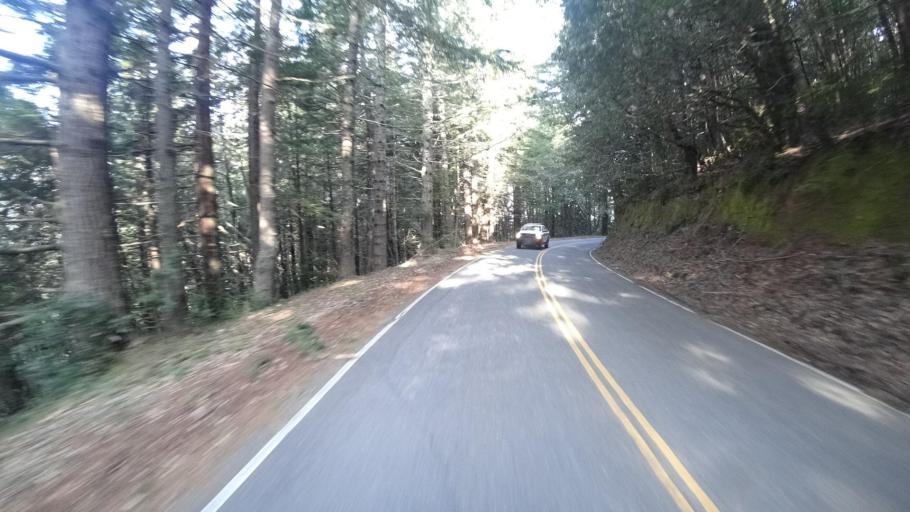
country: US
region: California
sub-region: Humboldt County
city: Bayside
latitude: 40.7502
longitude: -123.9821
